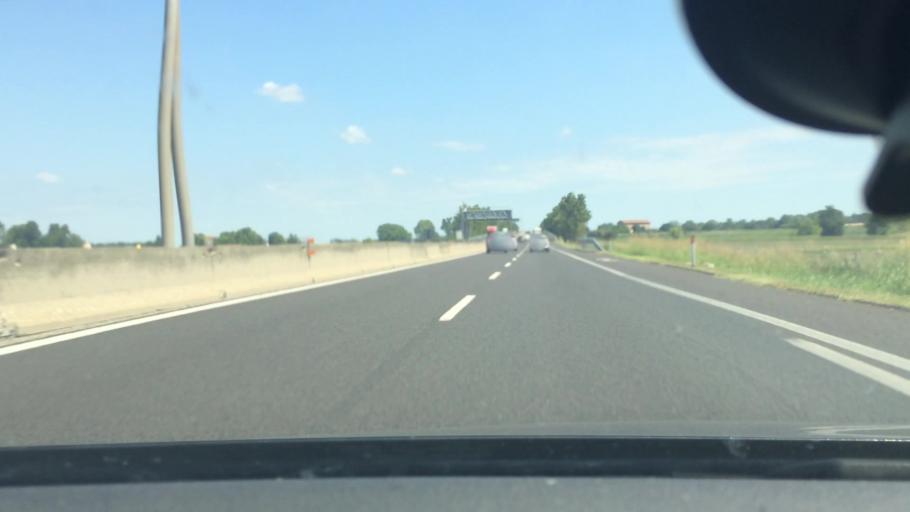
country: IT
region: Emilia-Romagna
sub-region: Provincia di Bologna
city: Altedo
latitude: 44.6905
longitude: 11.4820
